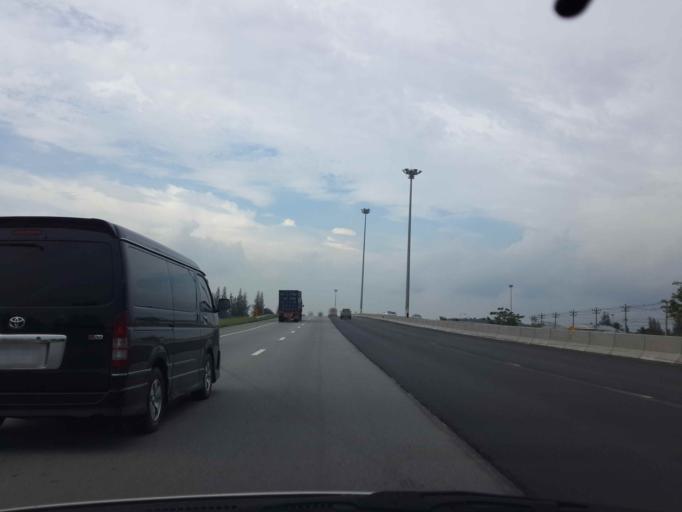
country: TH
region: Chon Buri
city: Chon Buri
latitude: 13.3436
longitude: 101.0271
